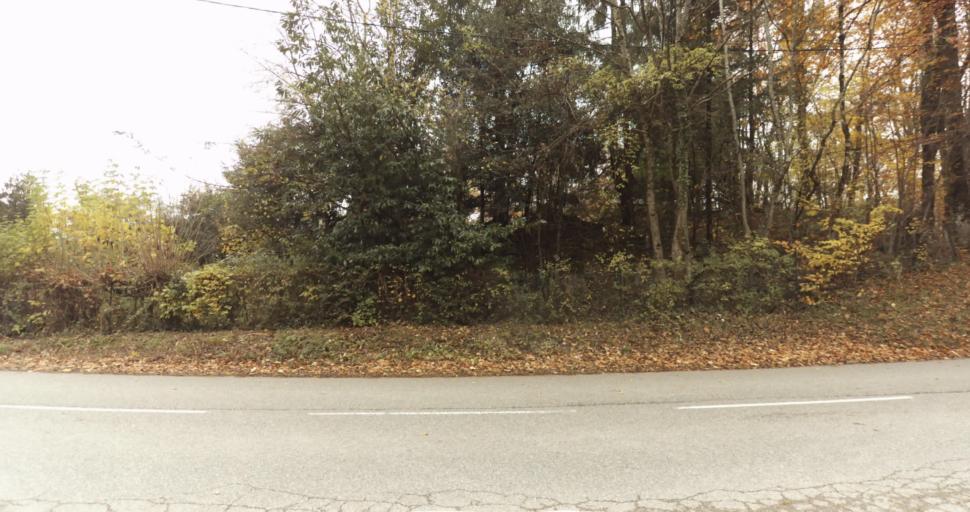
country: FR
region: Rhone-Alpes
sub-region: Departement de la Haute-Savoie
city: Annecy
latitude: 45.8901
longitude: 6.1327
